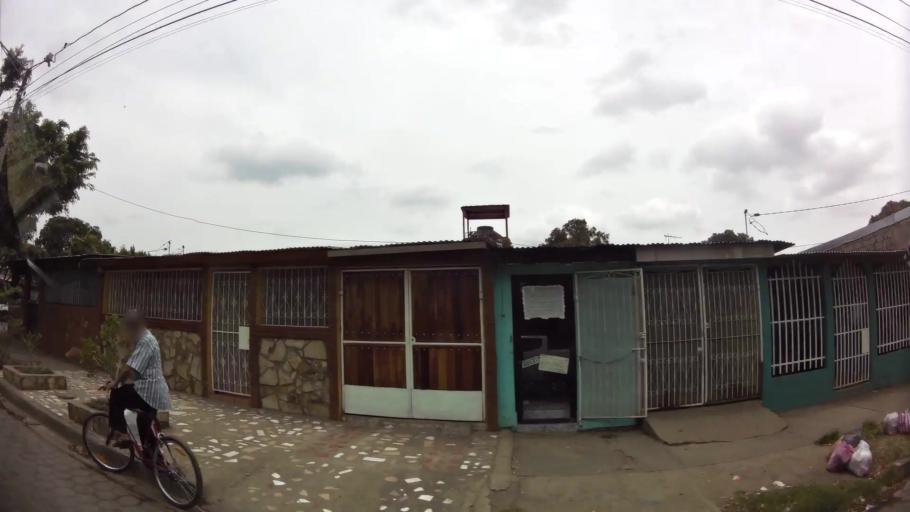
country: NI
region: Managua
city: Managua
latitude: 12.1242
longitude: -86.2173
